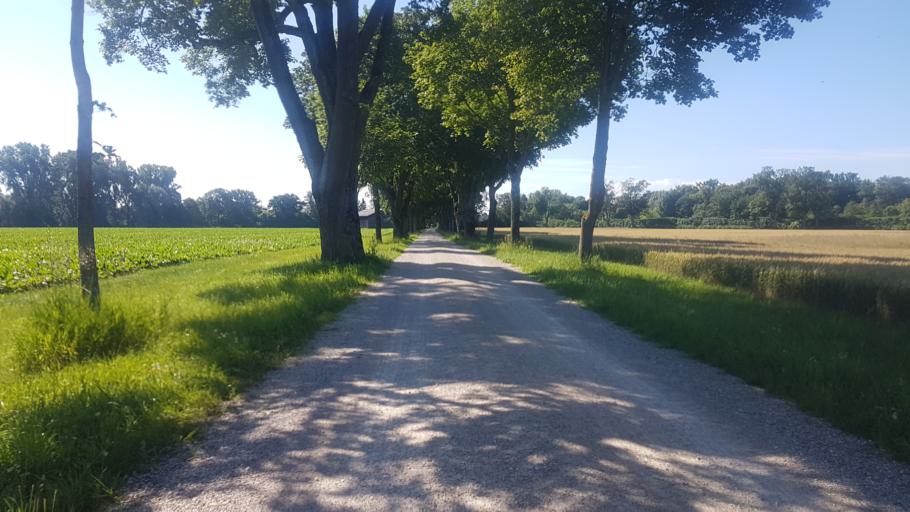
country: DE
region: Bavaria
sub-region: Upper Bavaria
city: Bergheim
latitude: 48.7306
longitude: 11.2700
